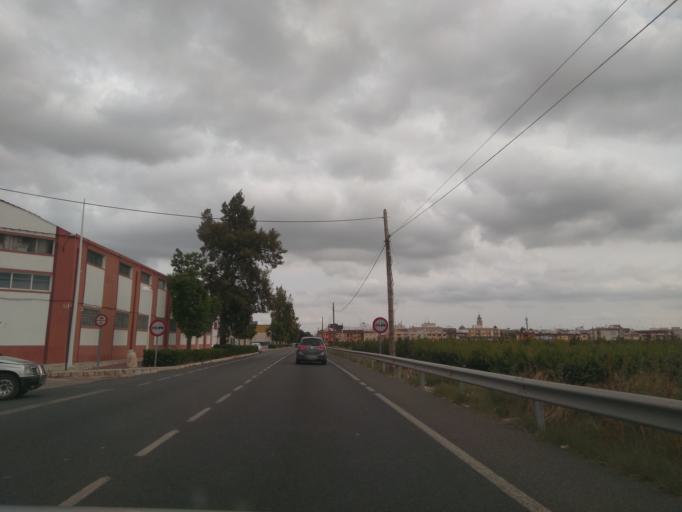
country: ES
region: Valencia
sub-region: Provincia de Valencia
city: L'Alcudia
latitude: 39.2049
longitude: -0.5082
